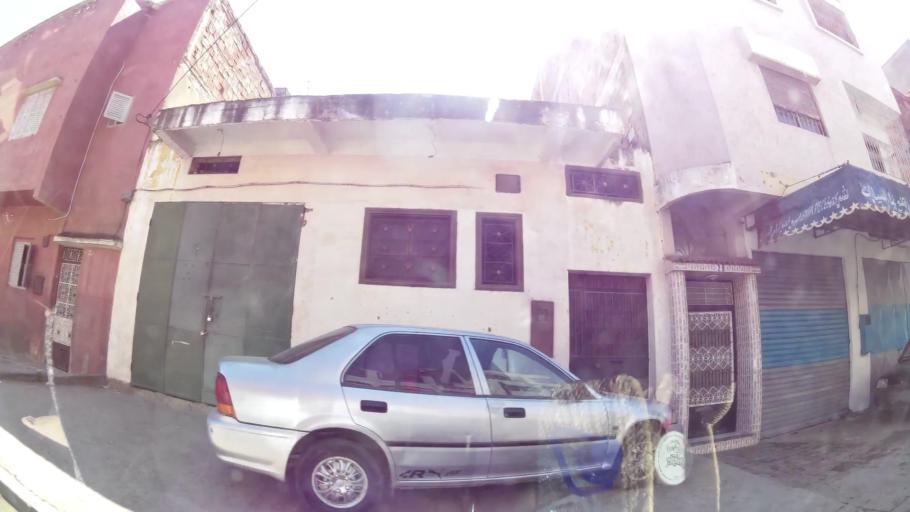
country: MA
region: Gharb-Chrarda-Beni Hssen
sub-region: Kenitra Province
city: Kenitra
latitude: 34.2433
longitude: -6.5549
